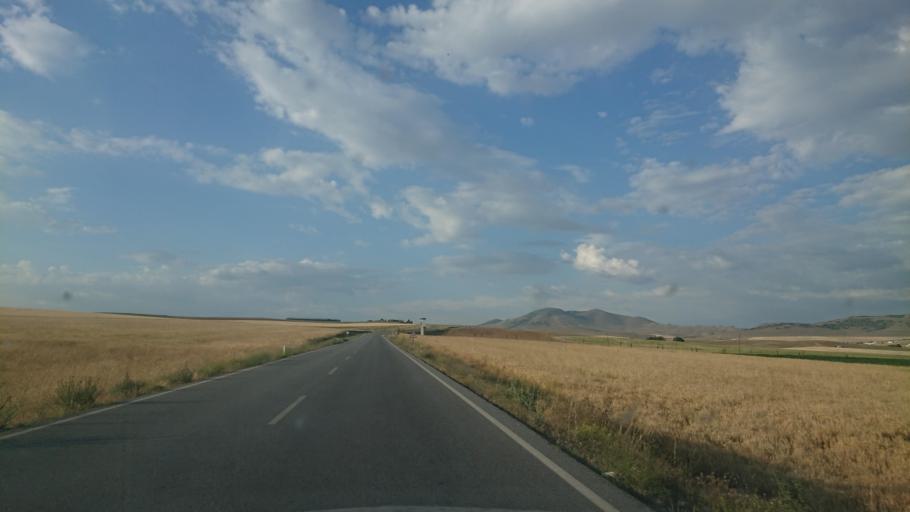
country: TR
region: Aksaray
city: Aksaray
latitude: 38.4960
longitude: 34.0738
